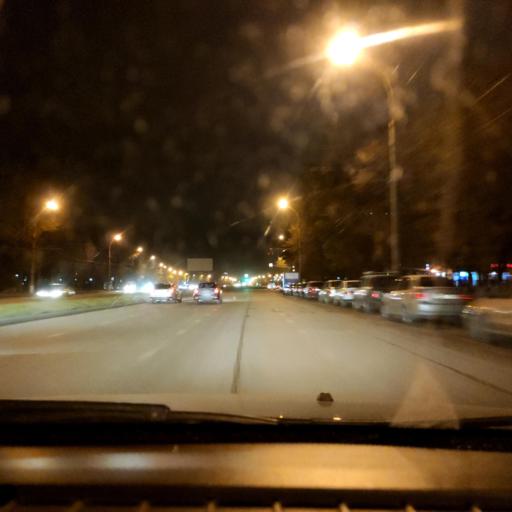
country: RU
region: Samara
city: Tol'yatti
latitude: 53.5173
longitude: 49.2584
